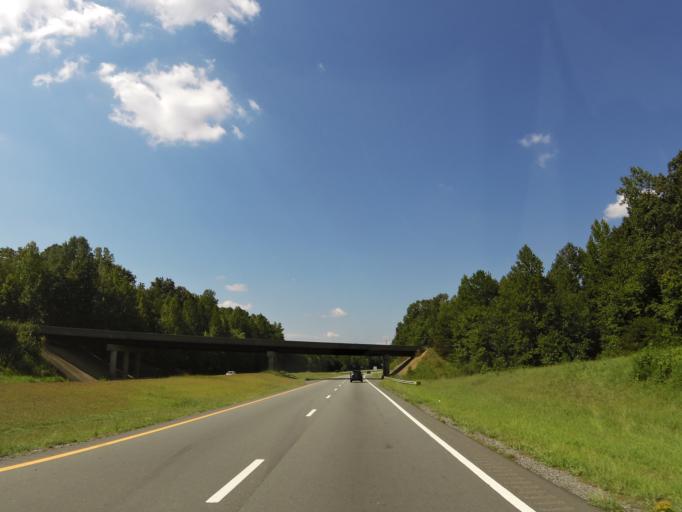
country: US
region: North Carolina
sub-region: Gaston County
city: Dallas
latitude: 35.3911
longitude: -81.2073
